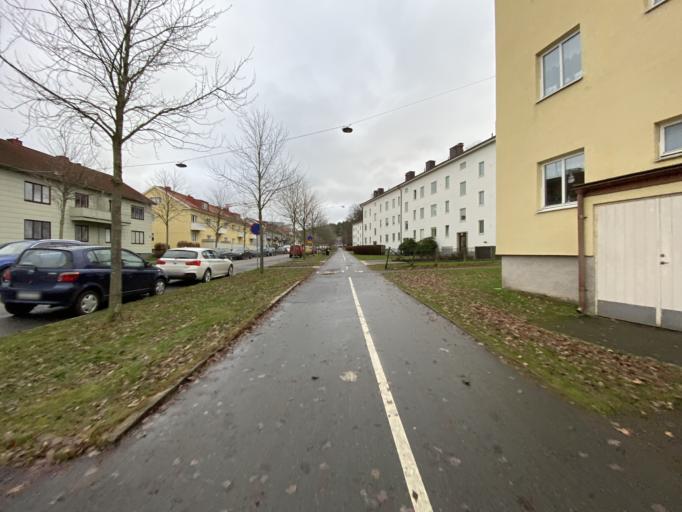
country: SE
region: Vaestra Goetaland
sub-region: Molndal
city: Moelndal
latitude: 57.7110
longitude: 12.0274
